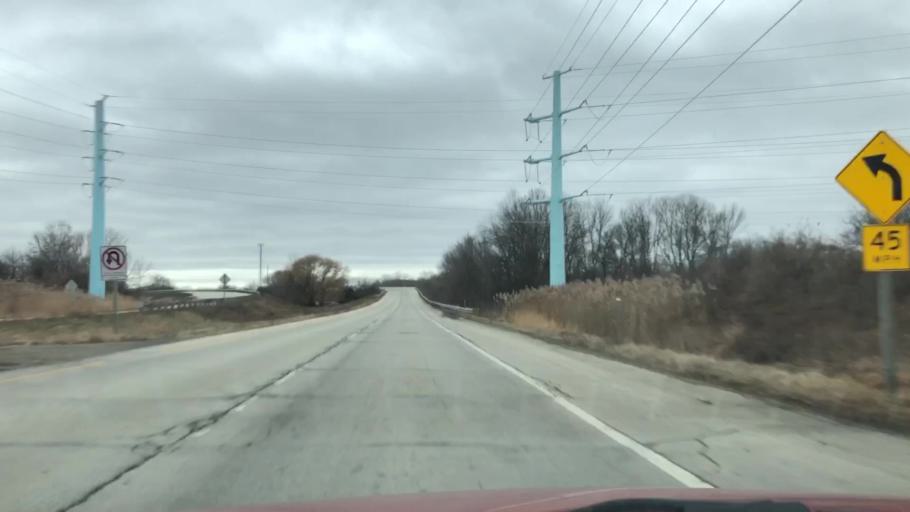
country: US
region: Wisconsin
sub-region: Brown County
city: De Pere
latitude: 44.4563
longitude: -88.0824
